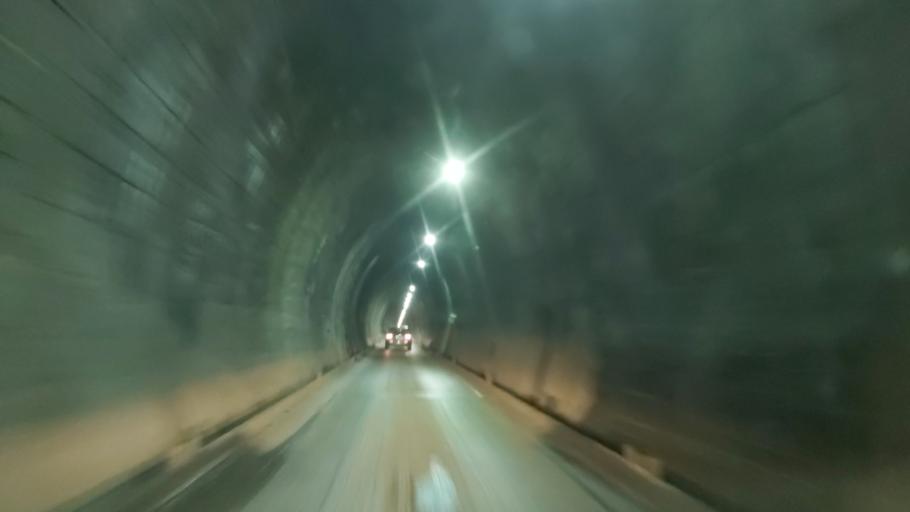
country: CL
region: Araucania
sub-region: Provincia de Cautin
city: Vilcun
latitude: -38.5236
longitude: -71.5138
